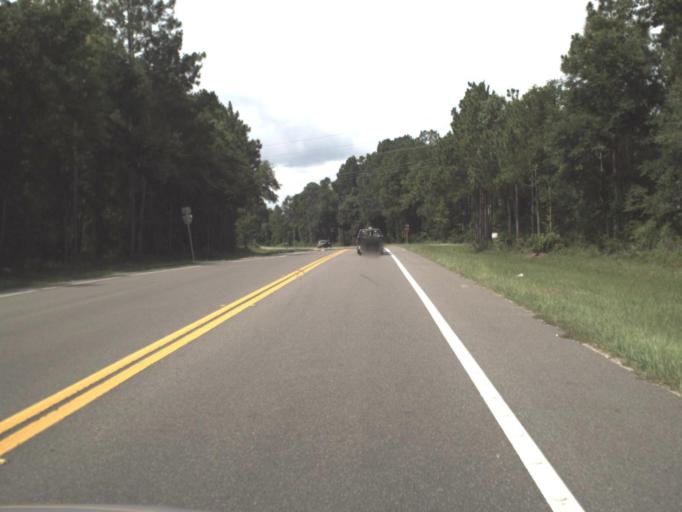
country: US
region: Florida
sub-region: Clay County
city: Keystone Heights
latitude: 29.8158
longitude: -82.0636
